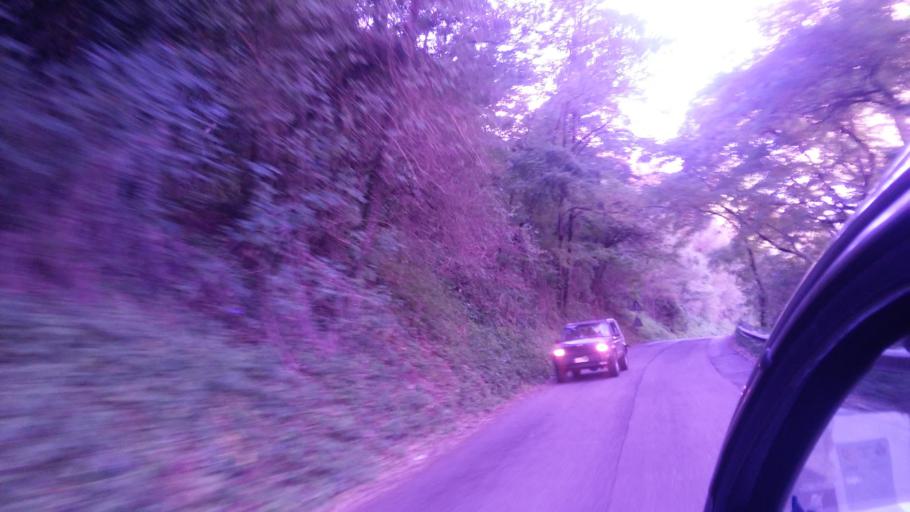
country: IT
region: Latium
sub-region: Provincia di Rieti
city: Amatrice
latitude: 42.6303
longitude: 13.2907
